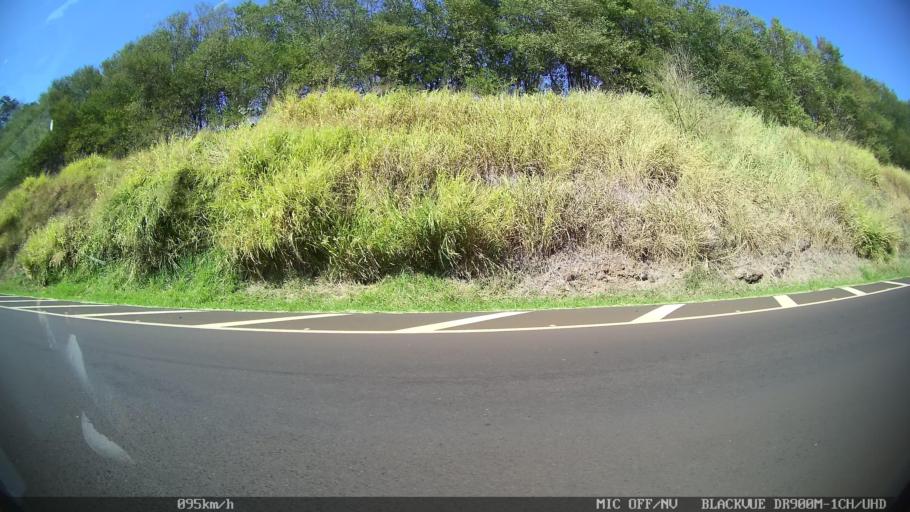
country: BR
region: Sao Paulo
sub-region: Franca
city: Franca
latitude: -20.5858
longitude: -47.4340
